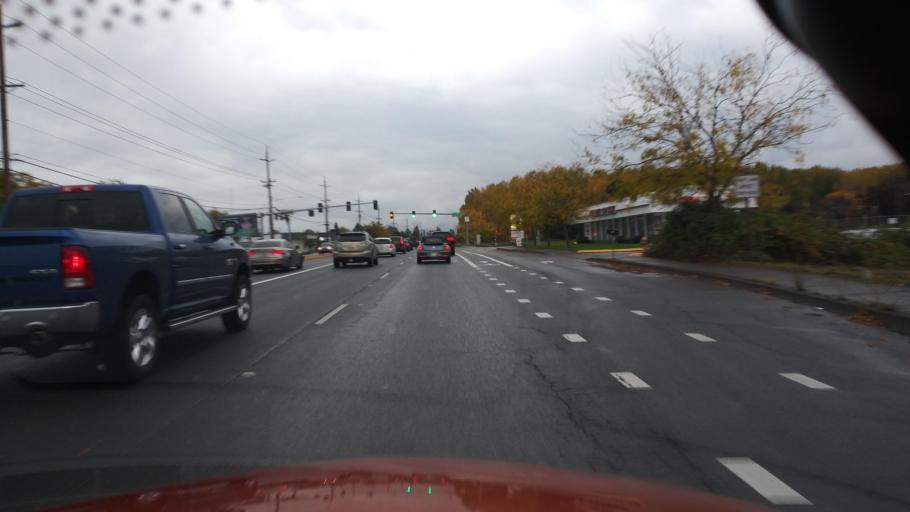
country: US
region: Oregon
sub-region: Washington County
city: Cornelius
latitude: 45.5201
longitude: -123.0384
